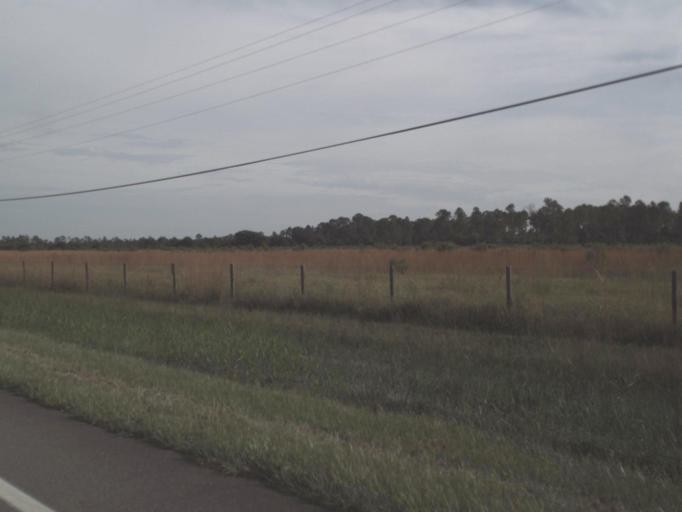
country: US
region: Florida
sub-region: Lee County
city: Olga
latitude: 26.8248
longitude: -81.7601
